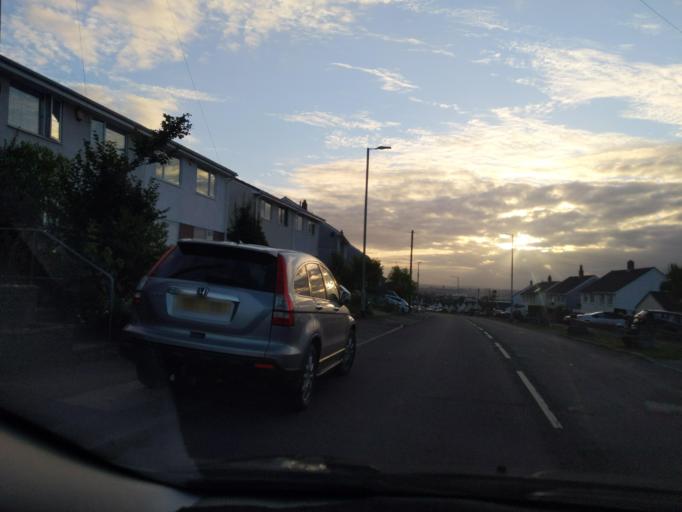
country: GB
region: England
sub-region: Plymouth
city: Plymstock
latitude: 50.3616
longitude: -4.0740
